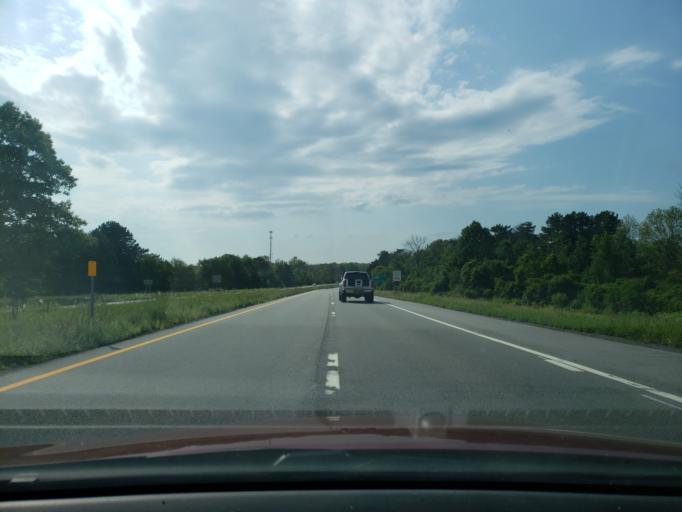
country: US
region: New York
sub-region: Monroe County
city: Greece
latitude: 43.2620
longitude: -77.6477
